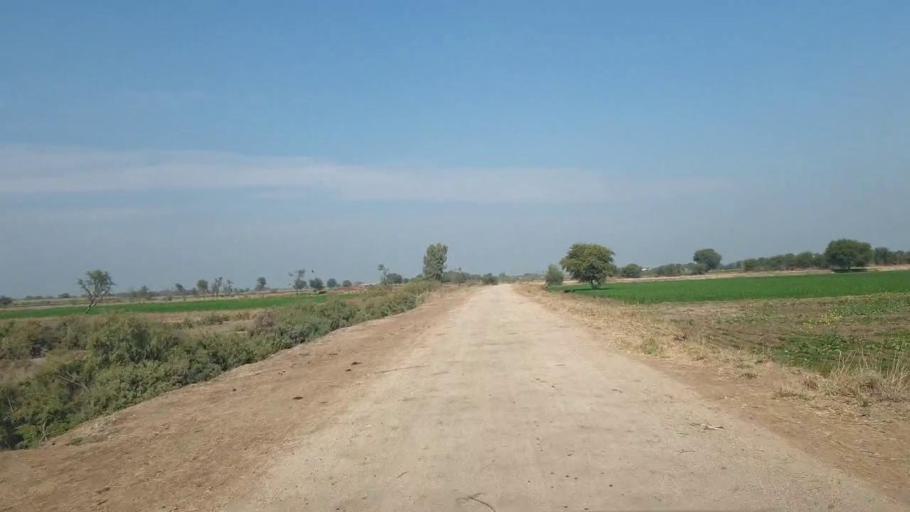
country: PK
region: Sindh
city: Shahdadpur
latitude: 25.9836
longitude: 68.5144
